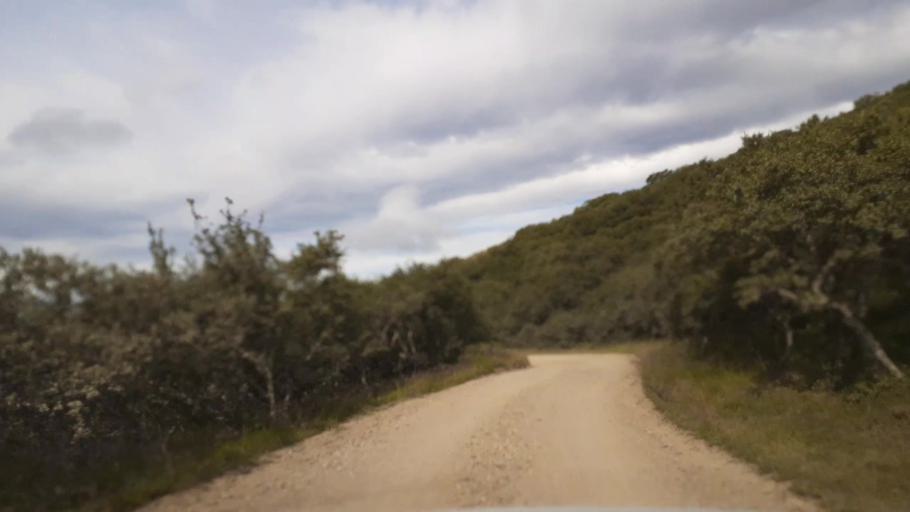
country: IS
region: East
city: Hoefn
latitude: 64.4395
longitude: -14.9173
